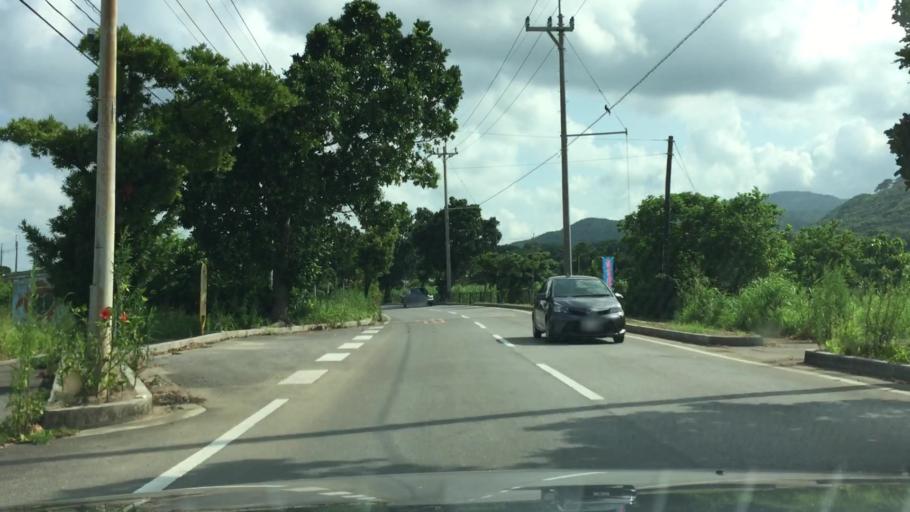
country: JP
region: Okinawa
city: Ishigaki
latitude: 24.4665
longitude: 124.2501
